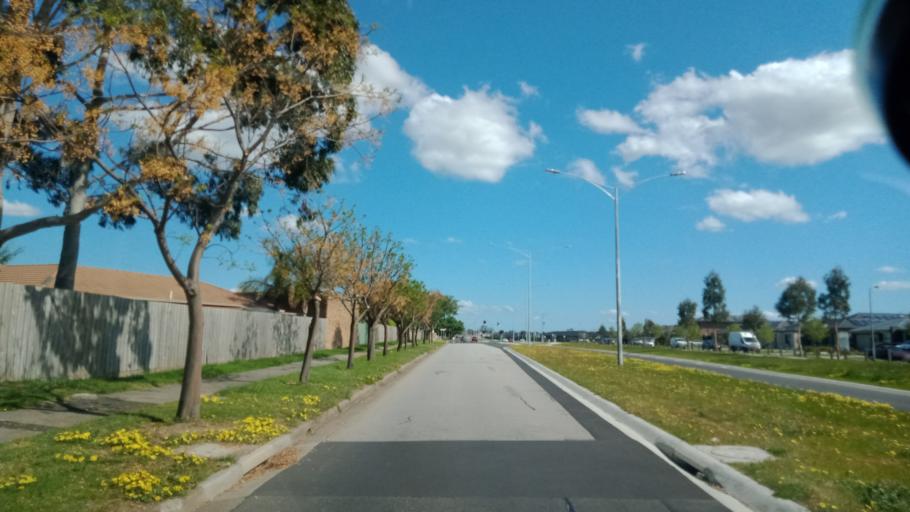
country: AU
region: Victoria
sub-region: Casey
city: Cranbourne West
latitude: -38.1001
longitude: 145.2543
